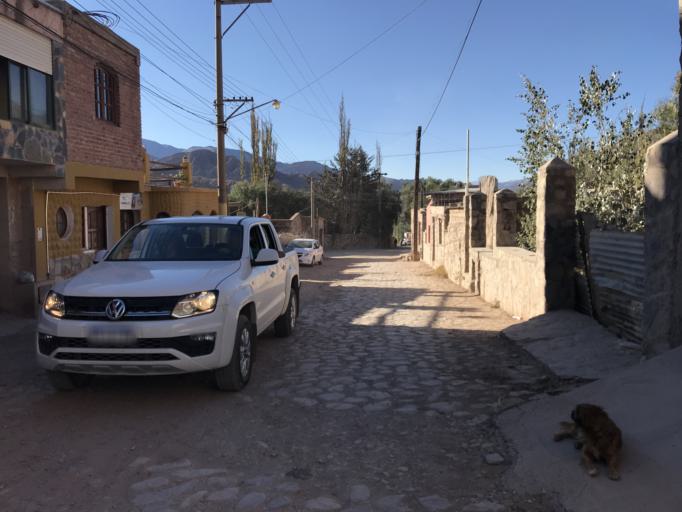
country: AR
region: Jujuy
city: Maimara
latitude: -23.5803
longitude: -65.3962
